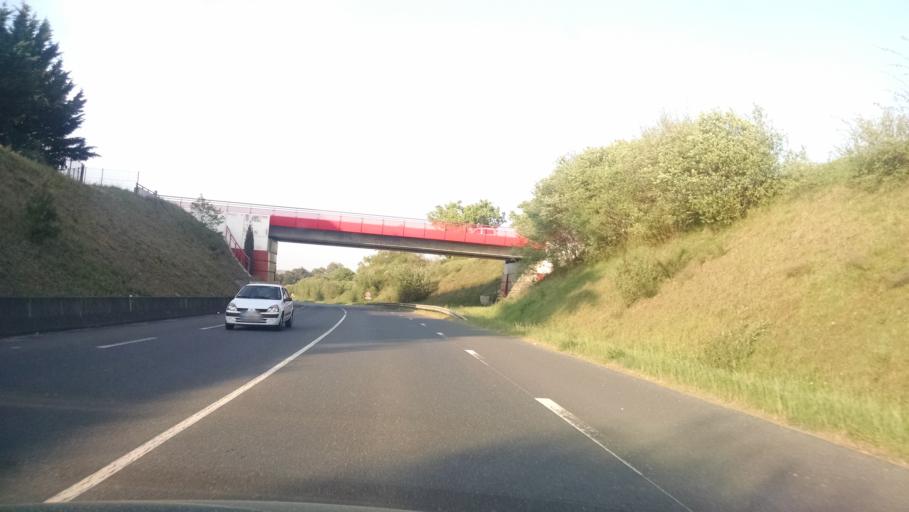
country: FR
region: Pays de la Loire
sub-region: Departement de la Loire-Atlantique
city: Gorges
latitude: 47.0953
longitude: -1.2937
